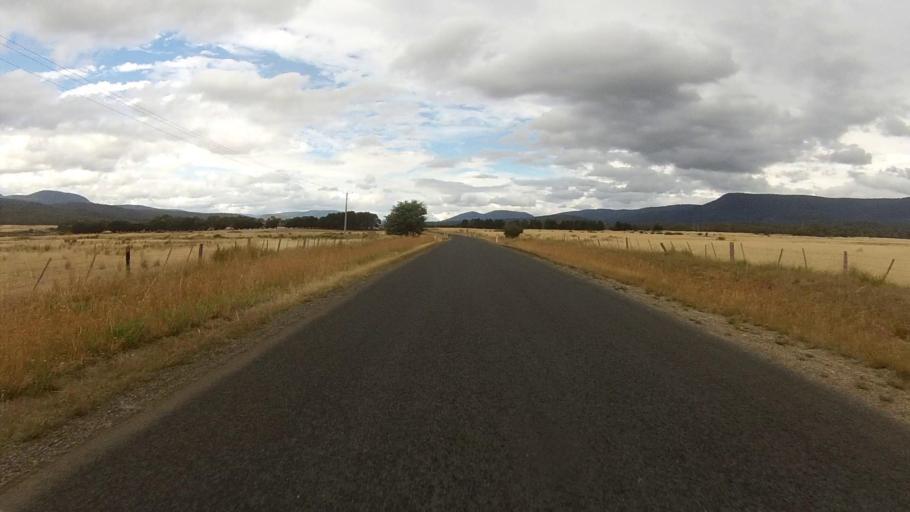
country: AU
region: Tasmania
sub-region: Break O'Day
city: St Helens
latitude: -41.8247
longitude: 147.8468
